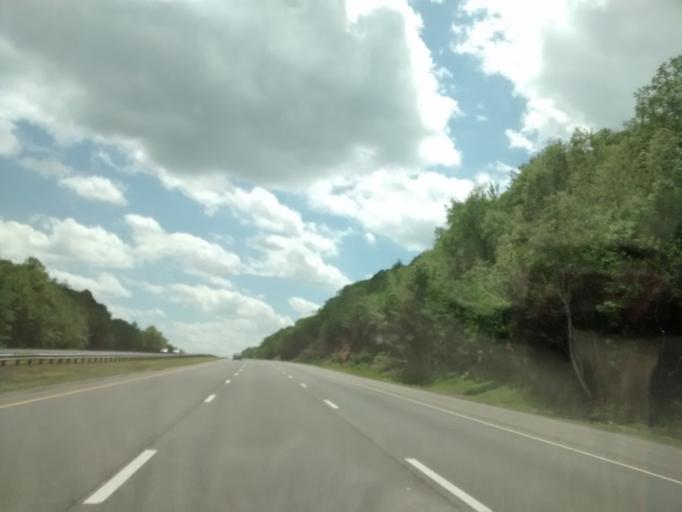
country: US
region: Massachusetts
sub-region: Hampden County
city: Holland
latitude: 42.0110
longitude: -72.1588
